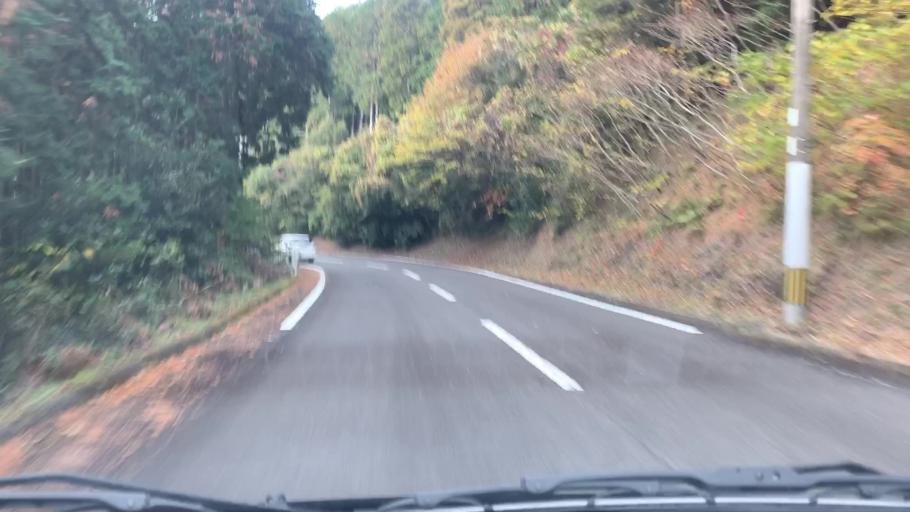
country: JP
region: Nagasaki
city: Togitsu
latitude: 32.9009
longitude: 129.7268
